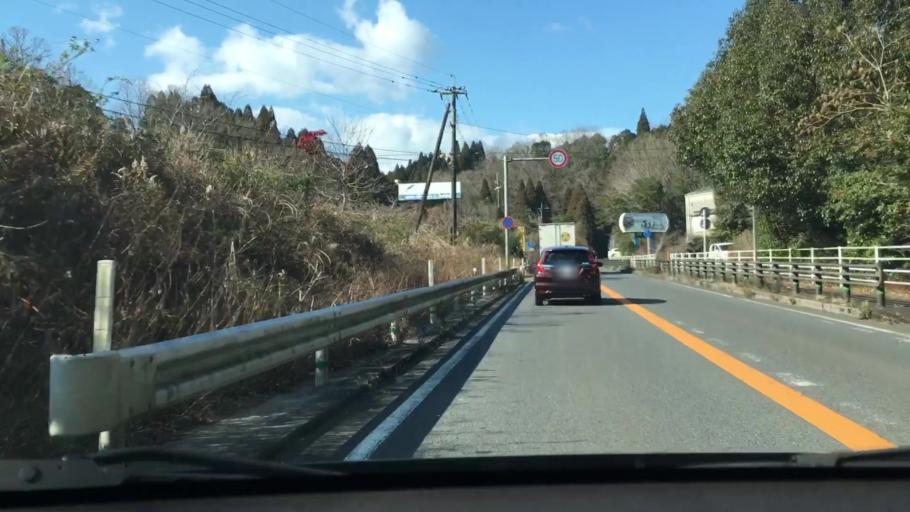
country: JP
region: Oita
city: Saiki
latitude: 32.9897
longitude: 131.8325
